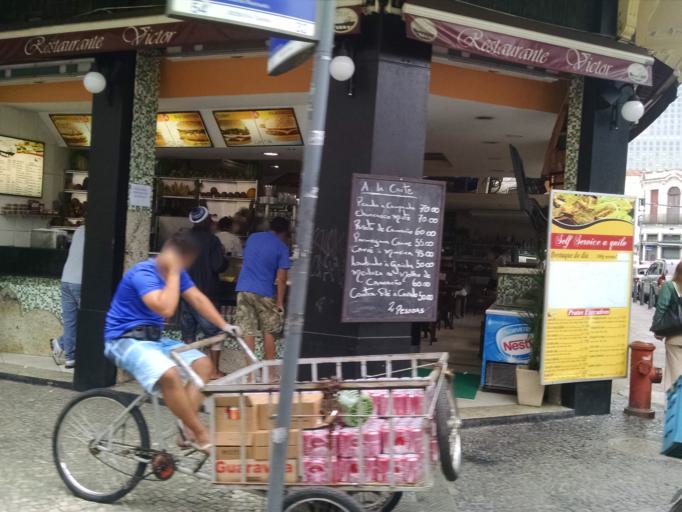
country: BR
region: Rio de Janeiro
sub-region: Rio De Janeiro
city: Rio de Janeiro
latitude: -22.9144
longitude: -43.1819
